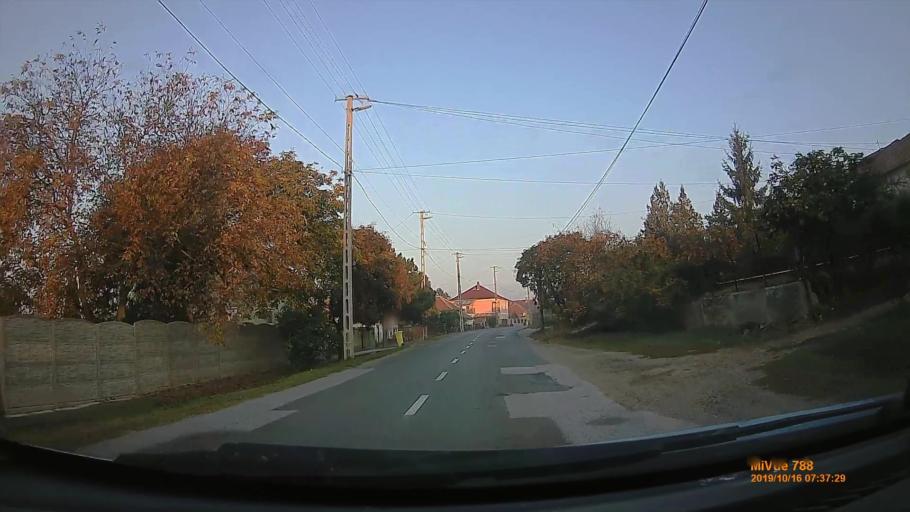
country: HU
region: Heves
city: Kerecsend
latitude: 47.7919
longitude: 20.3505
